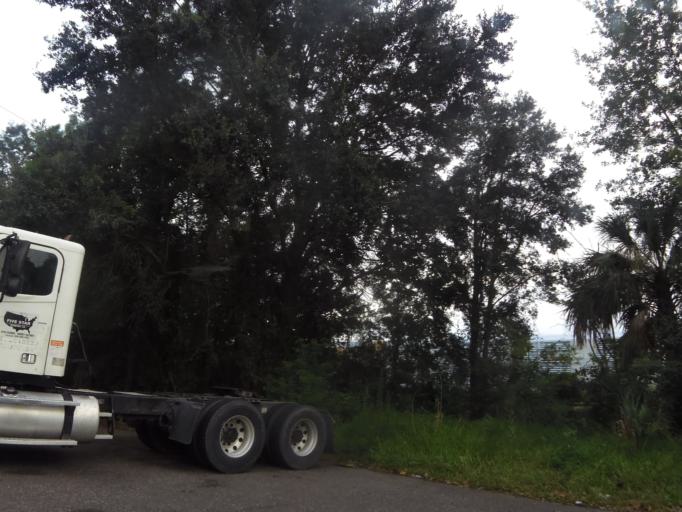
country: US
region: Florida
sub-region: Duval County
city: Jacksonville
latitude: 30.3492
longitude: -81.7037
